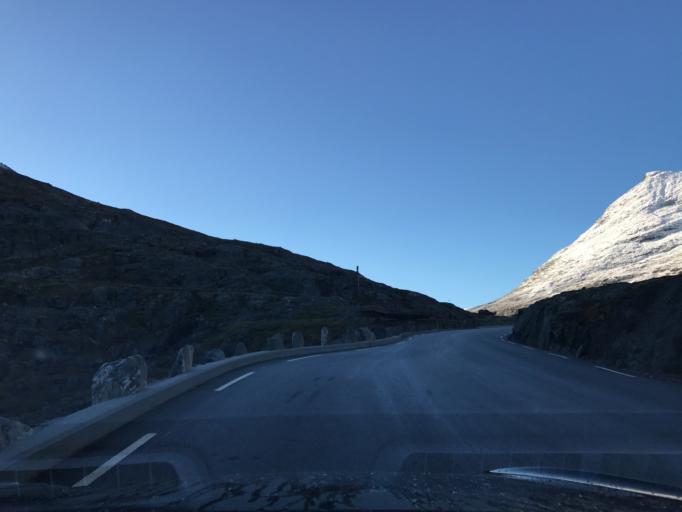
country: NO
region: More og Romsdal
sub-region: Rauma
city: Andalsnes
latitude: 62.4561
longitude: 7.6674
